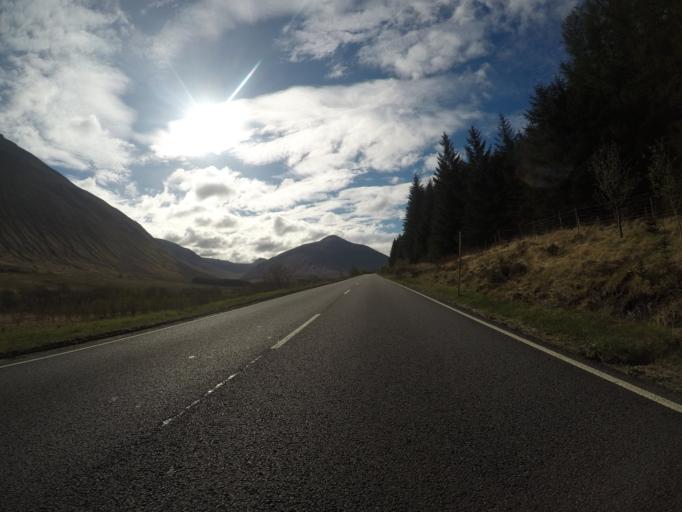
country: GB
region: Scotland
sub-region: Argyll and Bute
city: Garelochhead
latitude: 56.4948
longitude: -4.7538
